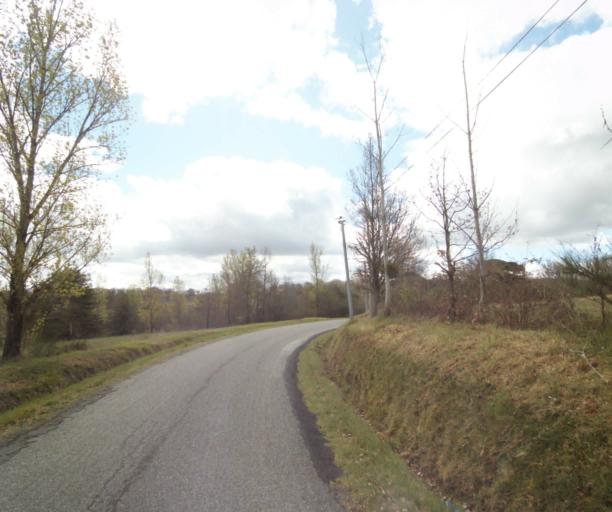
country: FR
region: Midi-Pyrenees
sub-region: Departement de l'Ariege
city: Saverdun
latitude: 43.2061
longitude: 1.5751
